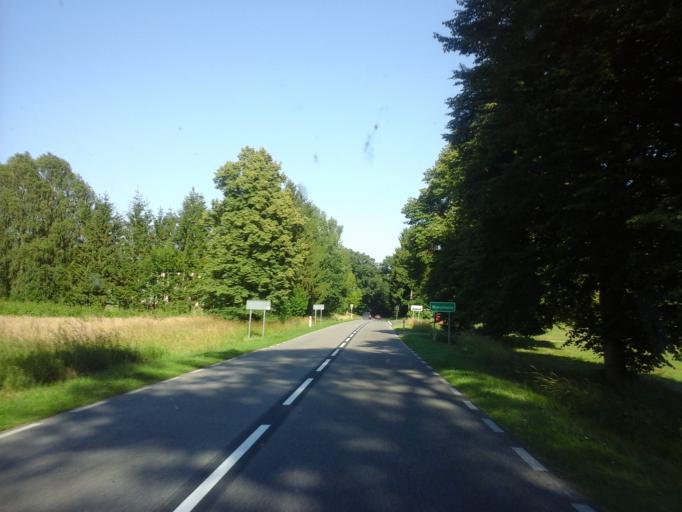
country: PL
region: West Pomeranian Voivodeship
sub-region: Powiat goleniowski
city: Nowogard
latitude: 53.6501
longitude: 15.2141
